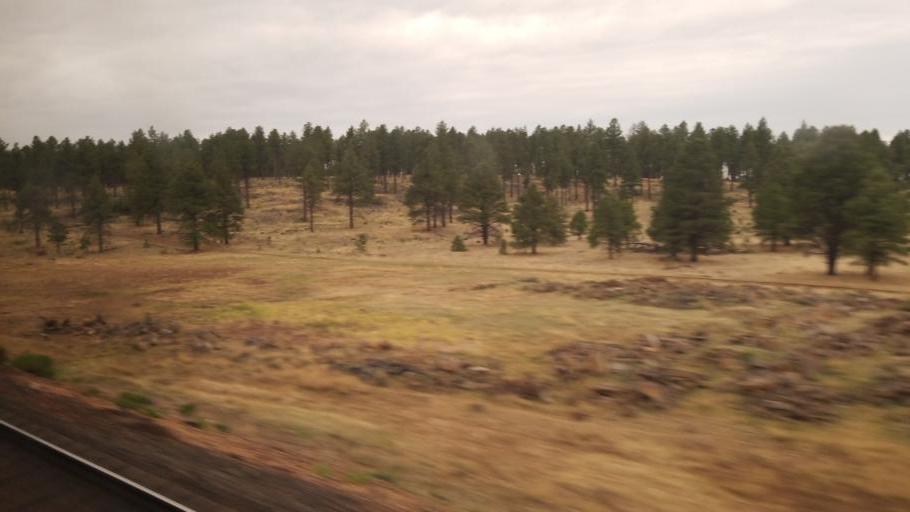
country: US
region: Arizona
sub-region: Coconino County
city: Parks
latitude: 35.2333
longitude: -112.0239
